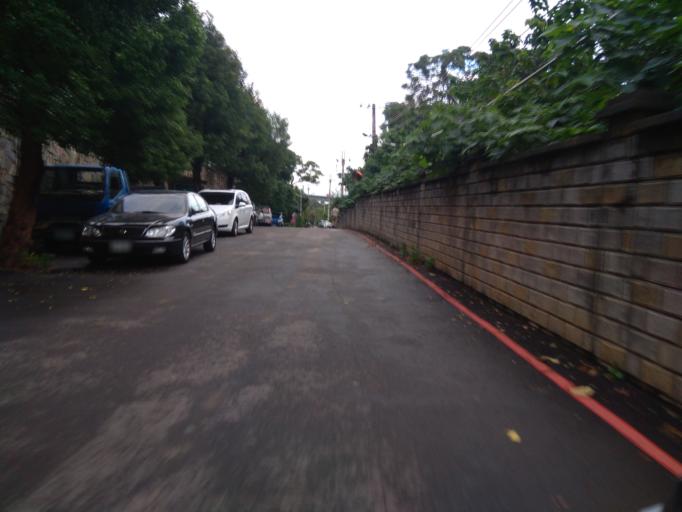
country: TW
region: Taiwan
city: Taoyuan City
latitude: 24.9453
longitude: 121.1971
